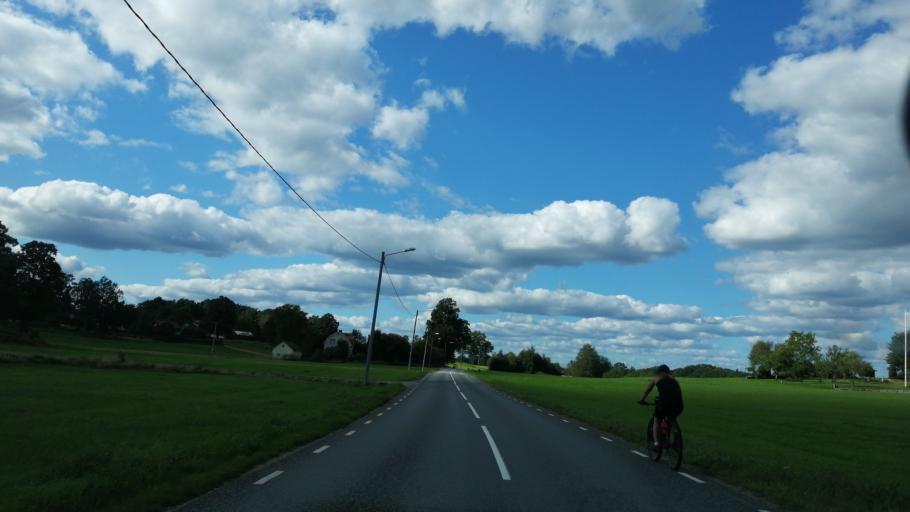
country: SE
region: Joenkoeping
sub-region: Gislaveds Kommun
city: Reftele
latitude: 57.1514
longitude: 13.6321
